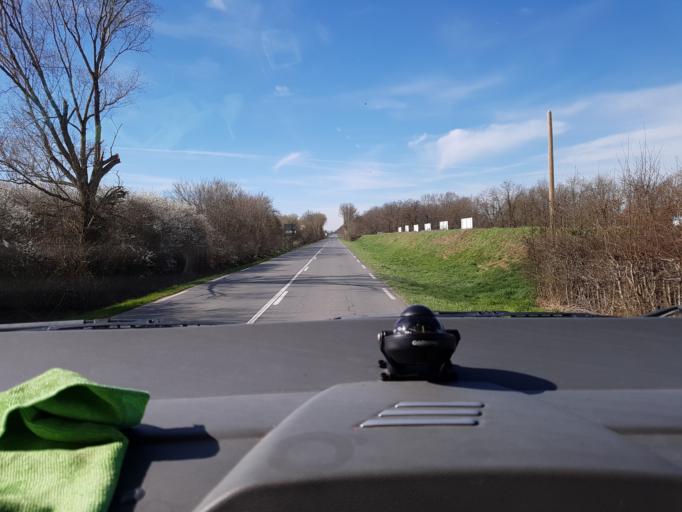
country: FR
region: Bourgogne
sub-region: Departement de Saone-et-Loire
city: Gueugnon
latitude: 46.5698
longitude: 4.0570
